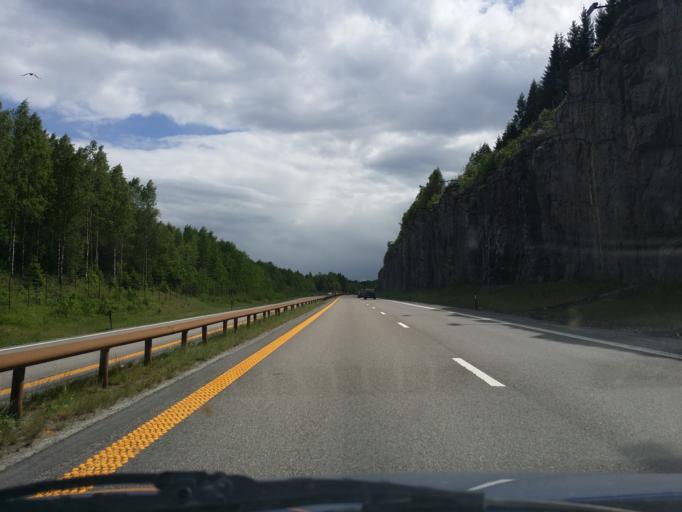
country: NO
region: Akershus
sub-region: Eidsvoll
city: Eidsvoll
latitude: 60.3565
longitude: 11.2062
